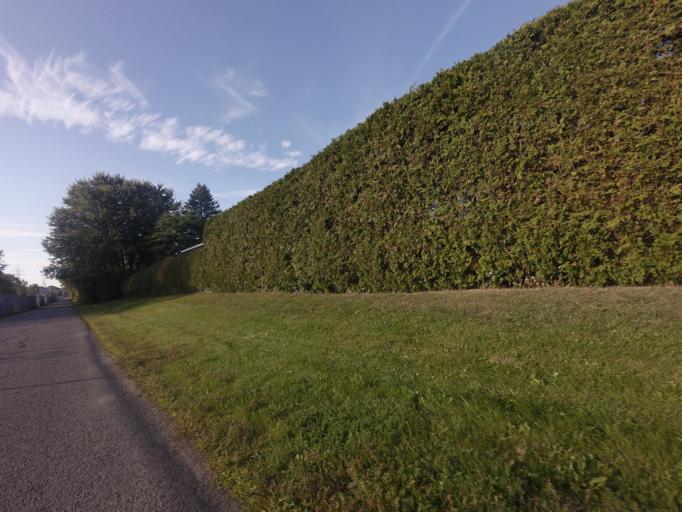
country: CA
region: Quebec
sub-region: Laurentides
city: Saint-Jerome
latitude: 45.7660
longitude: -73.9910
